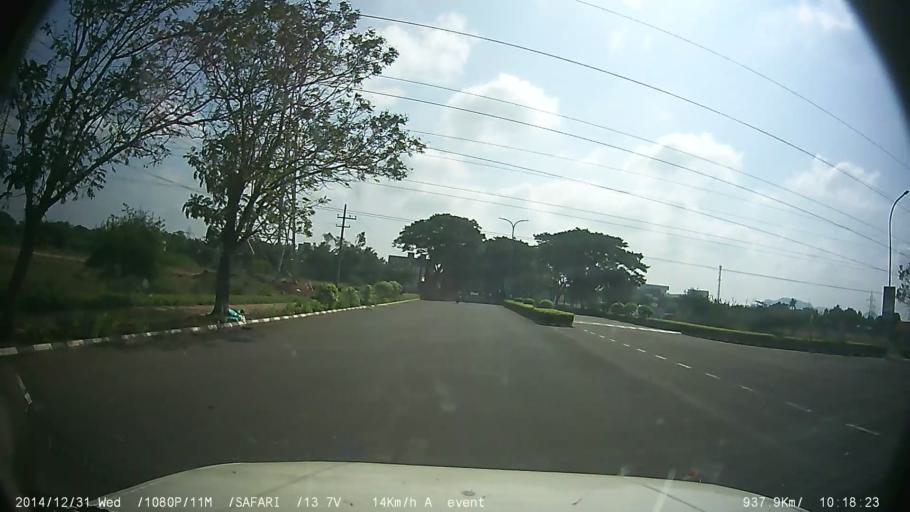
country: IN
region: Tamil Nadu
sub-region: Kancheepuram
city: Singapperumalkovil
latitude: 12.7399
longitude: 79.9971
